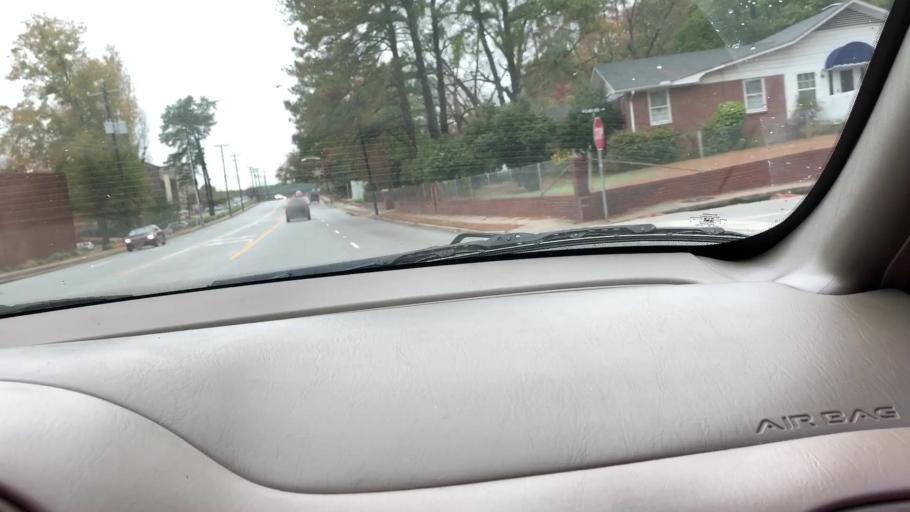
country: US
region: South Carolina
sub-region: Richland County
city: Forest Acres
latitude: 34.0201
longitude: -80.9852
